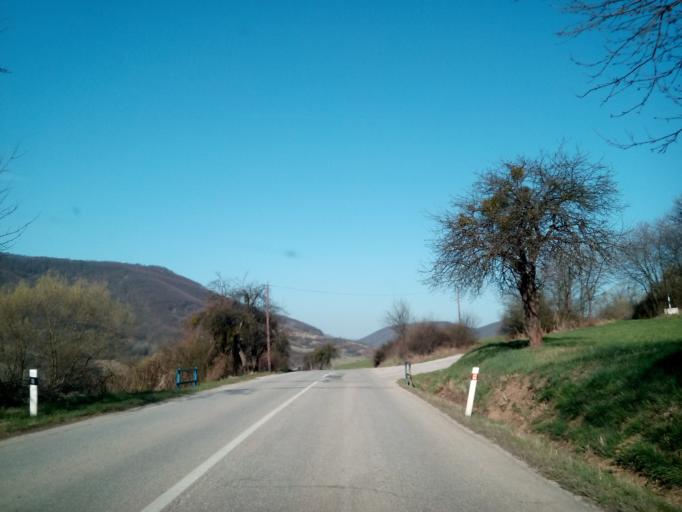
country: SK
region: Kosicky
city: Roznava
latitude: 48.6621
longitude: 20.4553
